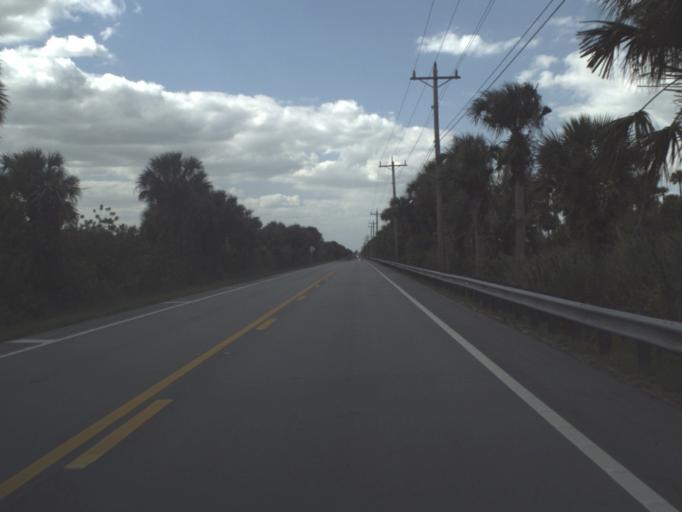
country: US
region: Florida
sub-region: Collier County
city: Marco
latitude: 25.9300
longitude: -81.4374
